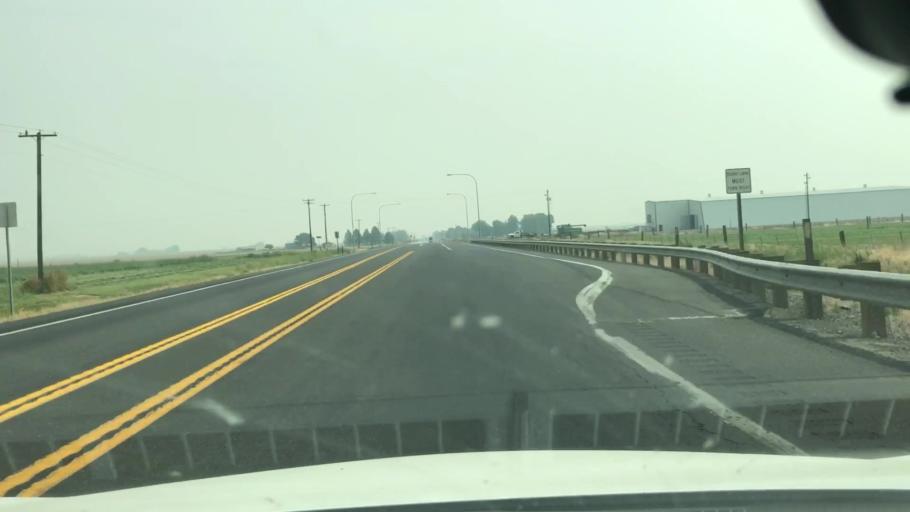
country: US
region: Washington
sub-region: Grant County
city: Quincy
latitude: 47.2342
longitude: -119.7707
